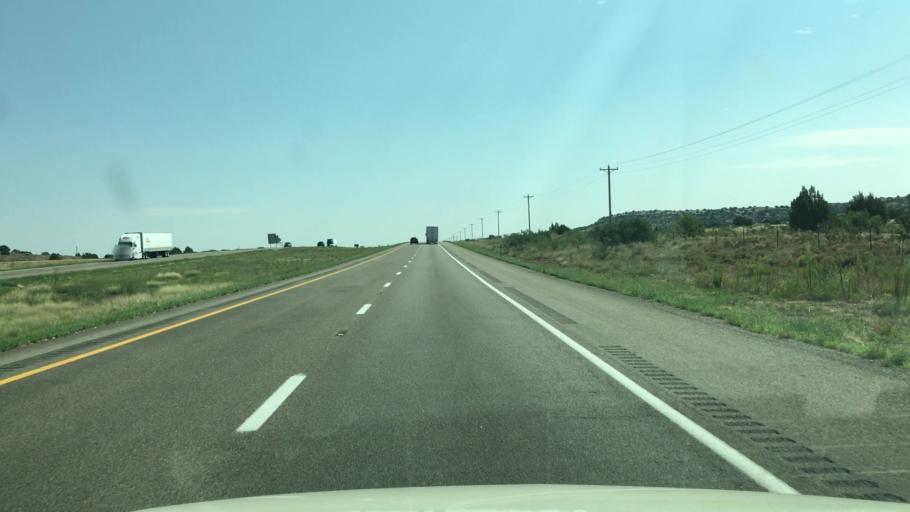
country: US
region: New Mexico
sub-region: Guadalupe County
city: Santa Rosa
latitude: 34.9568
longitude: -104.6202
